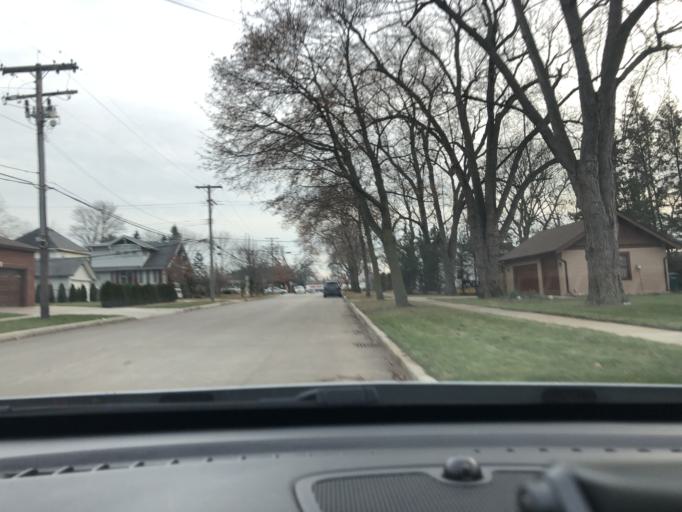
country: US
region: Michigan
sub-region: Wayne County
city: Dearborn Heights
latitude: 42.3062
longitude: -83.2543
